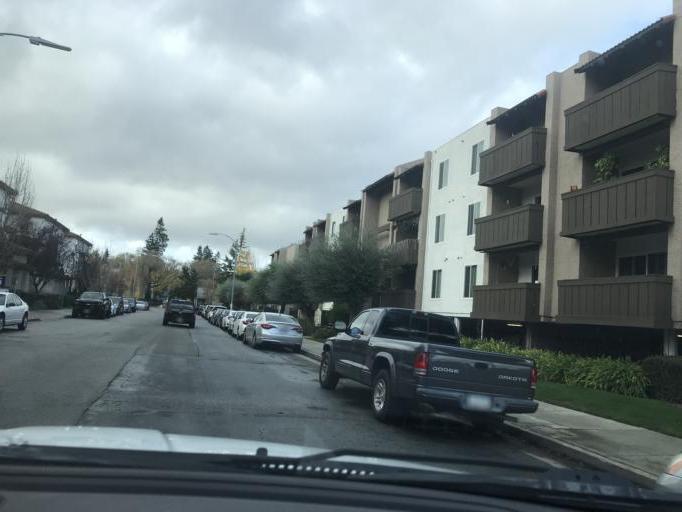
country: US
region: California
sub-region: Santa Clara County
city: Buena Vista
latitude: 37.3079
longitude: -121.9147
